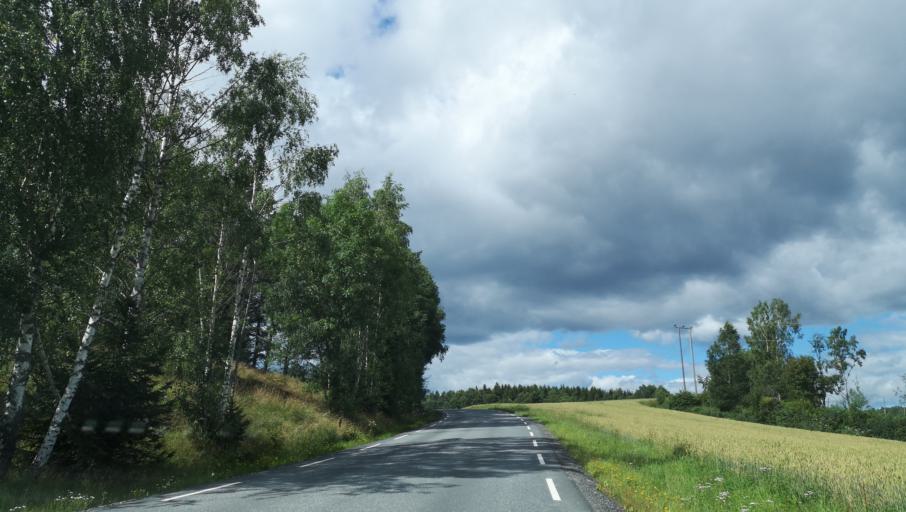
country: NO
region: Ostfold
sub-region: Hobol
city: Tomter
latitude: 59.6721
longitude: 10.9835
